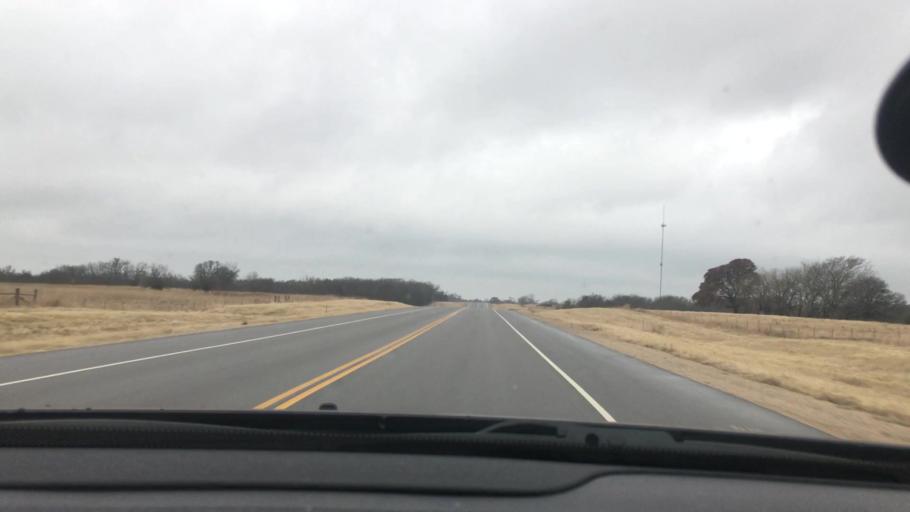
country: US
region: Oklahoma
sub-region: Johnston County
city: Tishomingo
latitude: 34.3255
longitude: -96.6627
